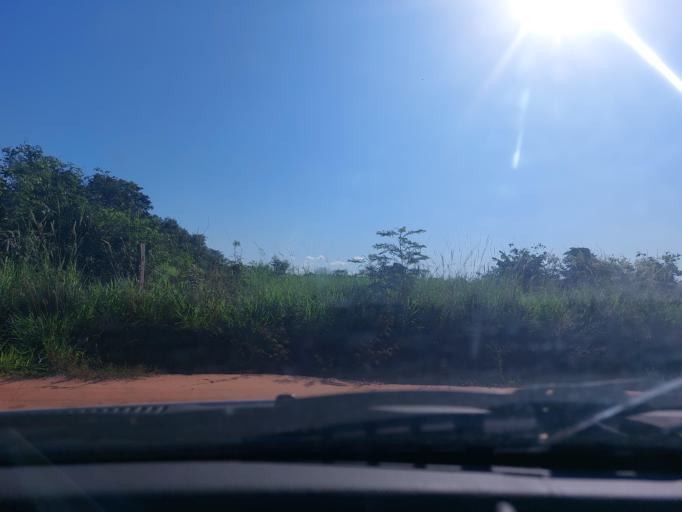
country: PY
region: San Pedro
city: Guayaybi
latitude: -24.5012
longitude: -56.5458
